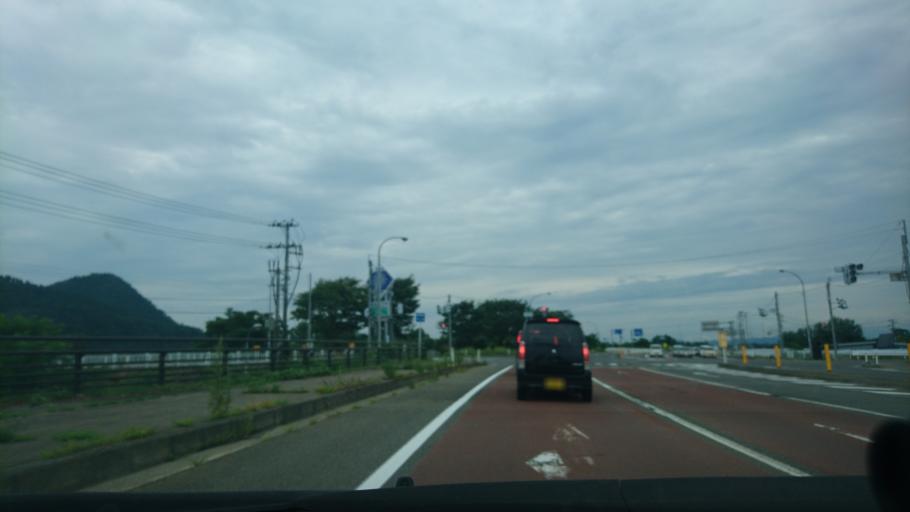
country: JP
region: Akita
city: Omagari
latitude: 39.4790
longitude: 140.4582
